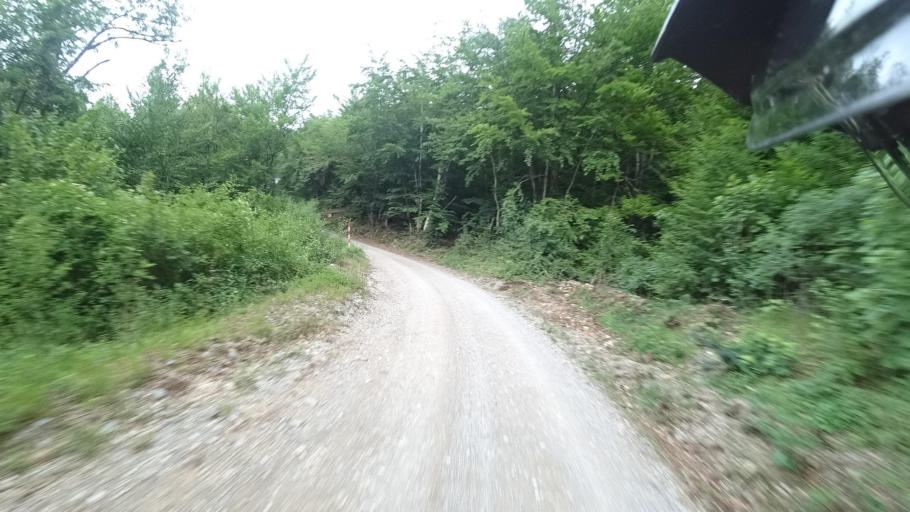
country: HR
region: Zadarska
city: Gracac
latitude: 44.5150
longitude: 15.8607
